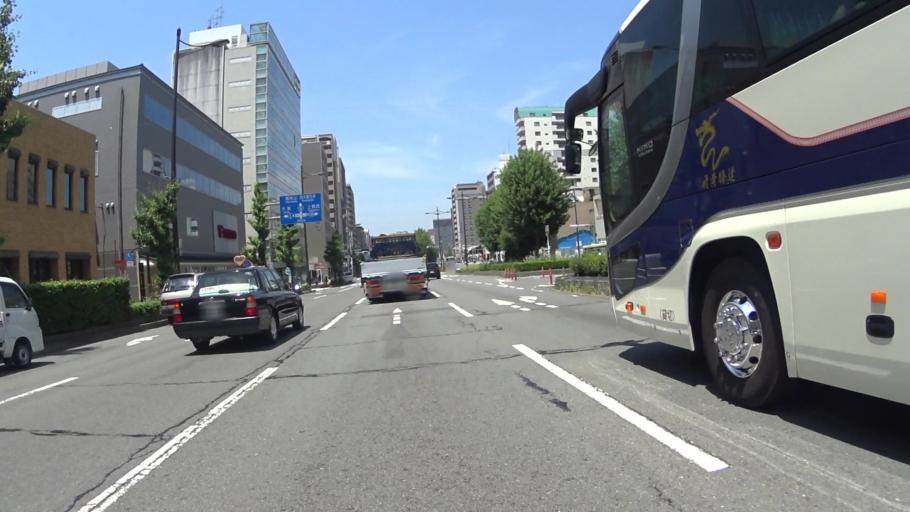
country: JP
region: Kyoto
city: Kyoto
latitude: 34.9962
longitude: 135.7560
